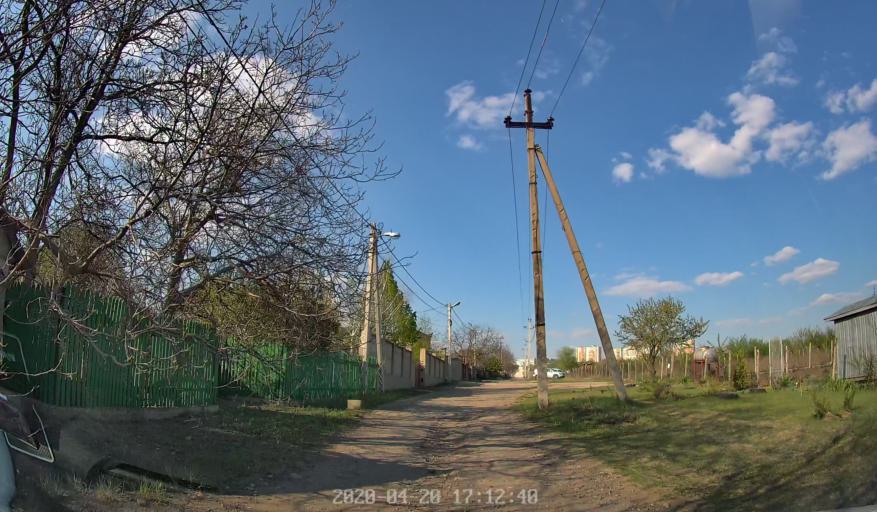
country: MD
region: Chisinau
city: Chisinau
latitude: 46.9654
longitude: 28.8420
